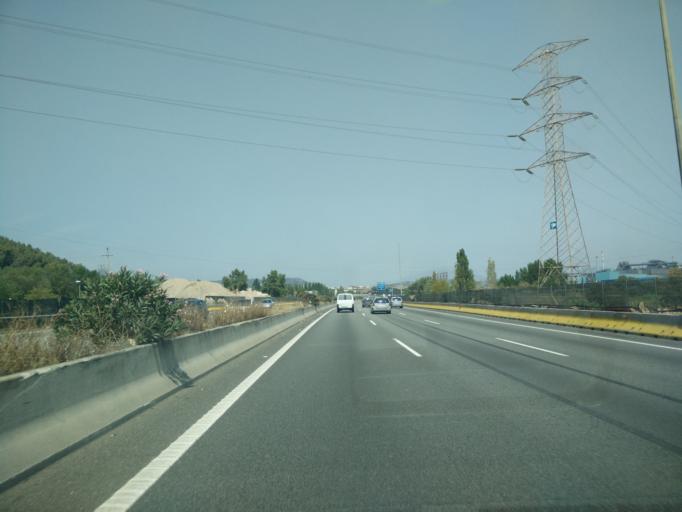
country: ES
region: Catalonia
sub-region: Provincia de Barcelona
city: Sant Andreu de la Barca
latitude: 41.4408
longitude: 1.9871
